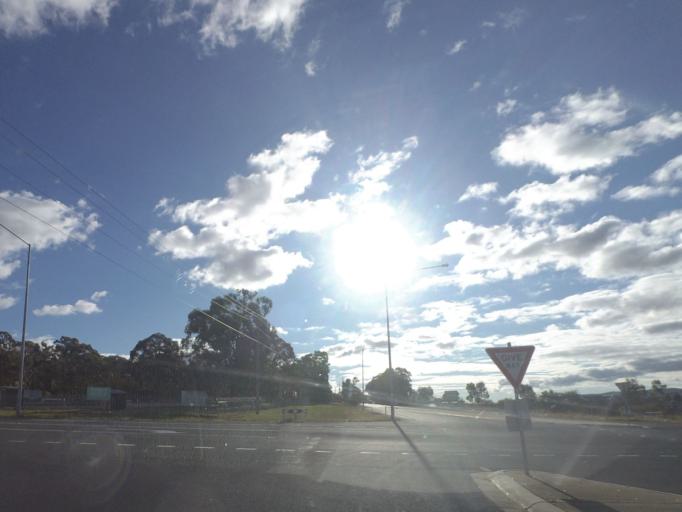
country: AU
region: Victoria
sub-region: Mount Alexander
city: Castlemaine
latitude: -37.0963
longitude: 144.3267
